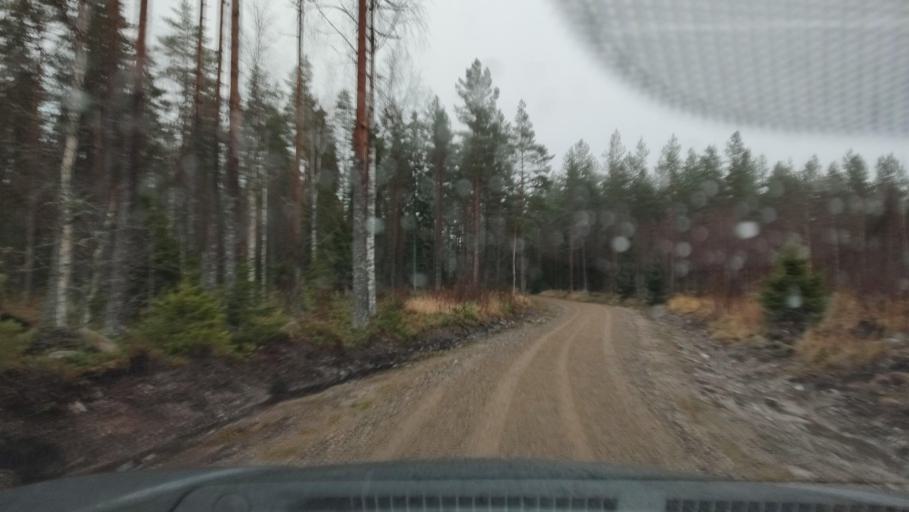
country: FI
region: Southern Ostrobothnia
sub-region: Suupohja
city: Karijoki
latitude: 62.1989
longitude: 21.7766
